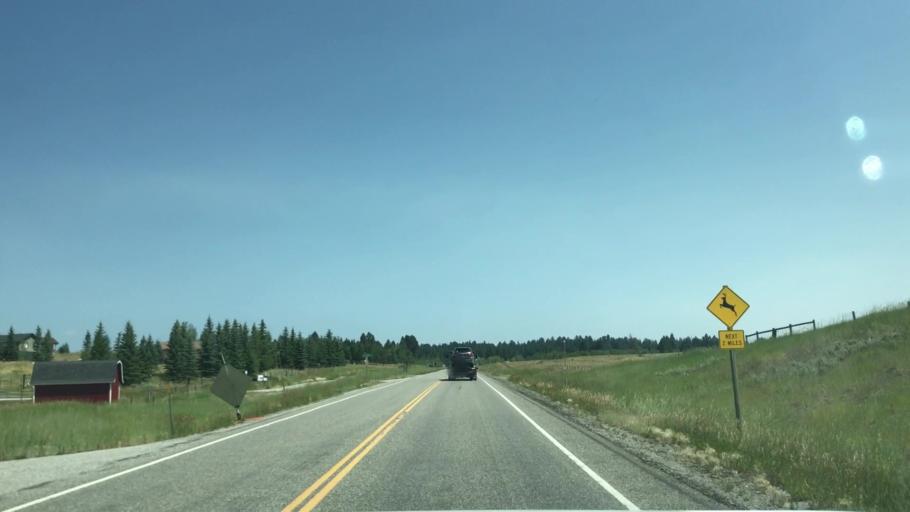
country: US
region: Montana
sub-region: Gallatin County
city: West Yellowstone
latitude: 44.7907
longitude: -111.1104
